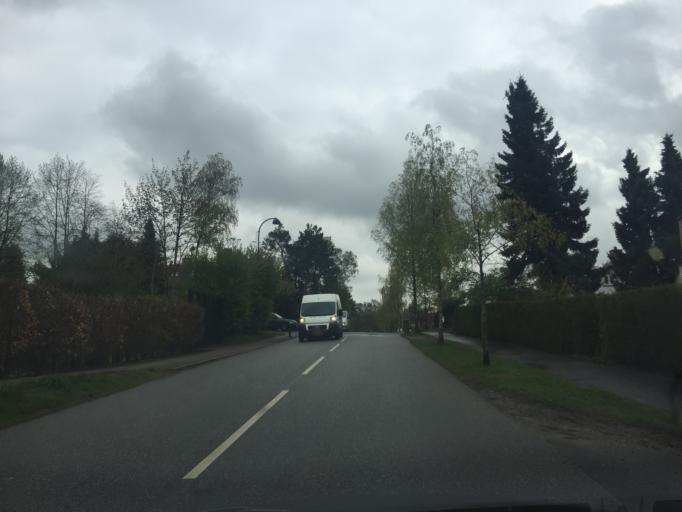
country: DK
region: Capital Region
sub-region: Rudersdal Kommune
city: Holte
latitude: 55.8031
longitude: 12.4506
